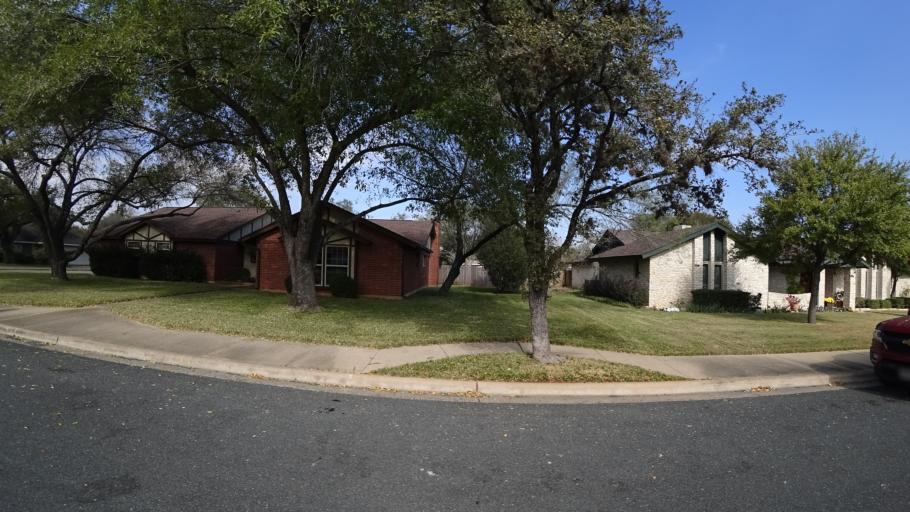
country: US
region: Texas
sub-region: Travis County
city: Shady Hollow
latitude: 30.1630
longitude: -97.8607
